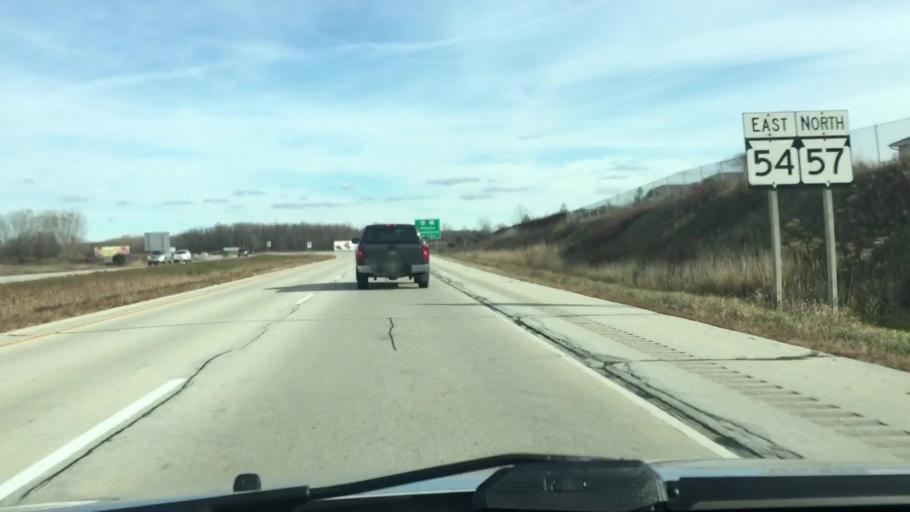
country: US
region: Wisconsin
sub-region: Brown County
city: Bellevue
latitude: 44.5240
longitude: -87.8959
